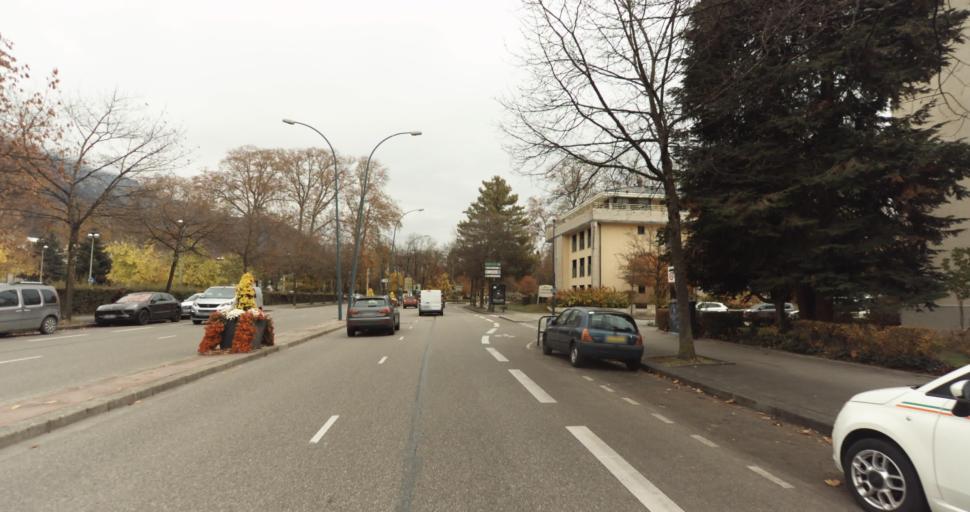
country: FR
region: Rhone-Alpes
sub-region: Departement de la Haute-Savoie
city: Annecy-le-Vieux
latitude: 45.9060
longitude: 6.1418
